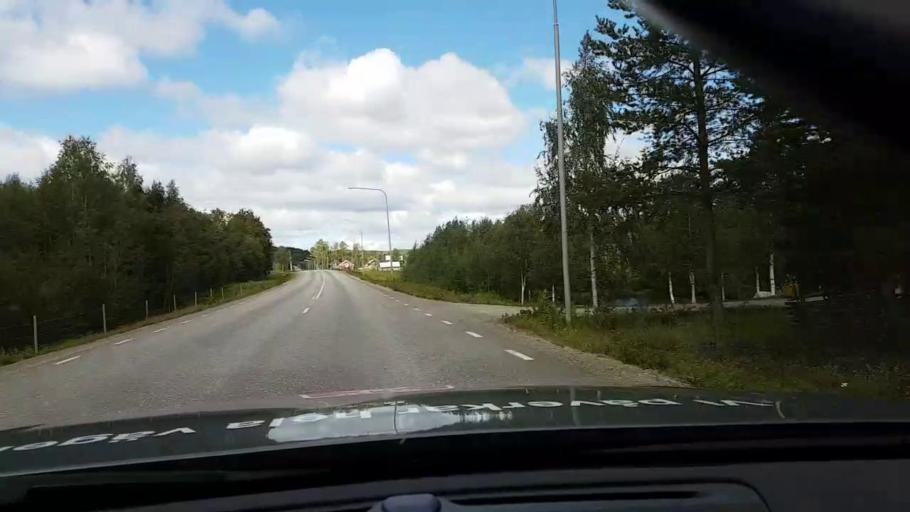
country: SE
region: Vaesternorrland
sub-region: OErnskoeldsviks Kommun
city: Bredbyn
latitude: 63.4780
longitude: 18.0936
